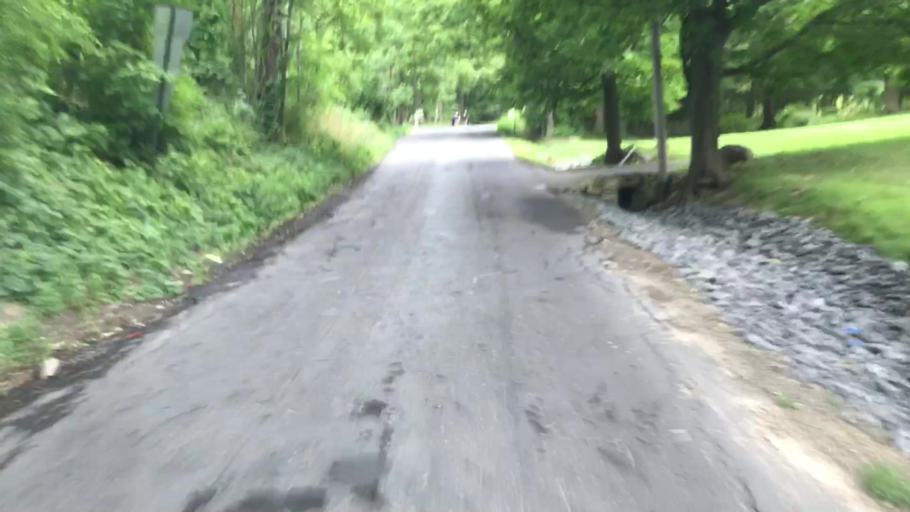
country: US
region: New York
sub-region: Onondaga County
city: Elbridge
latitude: 43.0061
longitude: -76.4541
